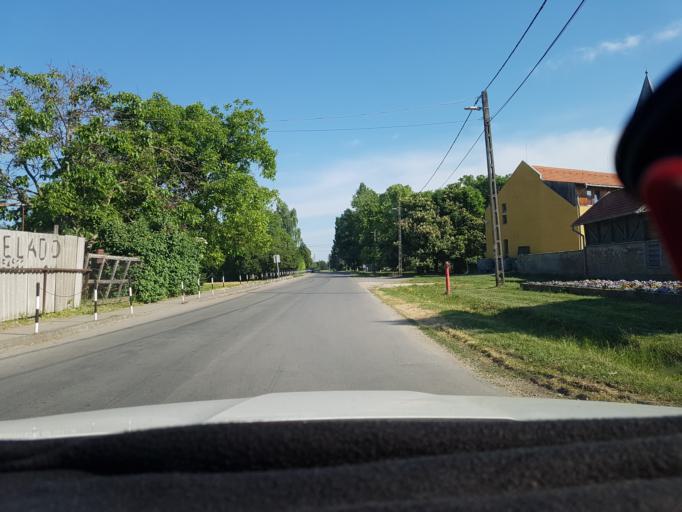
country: HU
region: Tolna
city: Decs
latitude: 46.2827
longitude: 18.7567
